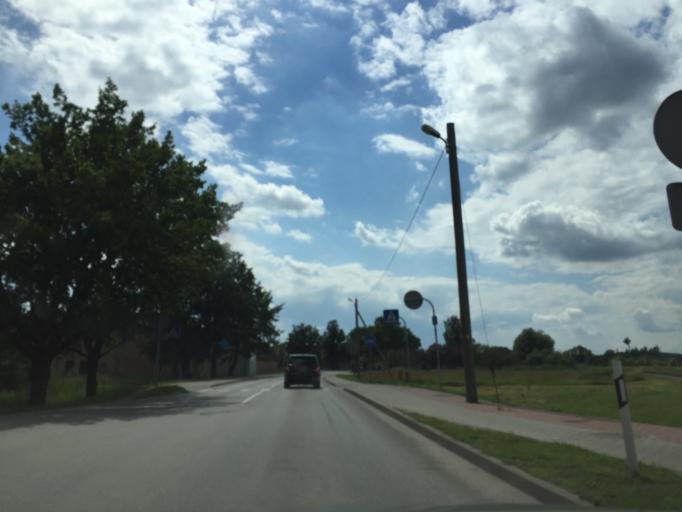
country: LV
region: Jelgava
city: Jelgava
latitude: 56.6324
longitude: 23.7038
